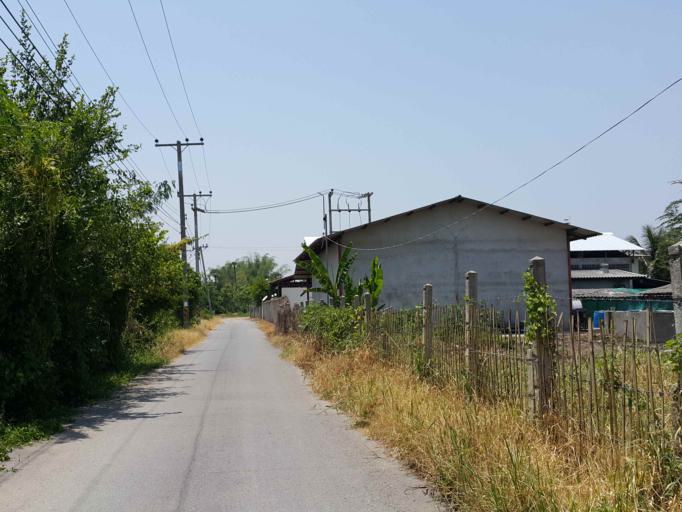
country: TH
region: Chiang Mai
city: San Sai
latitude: 18.8252
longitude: 99.1080
